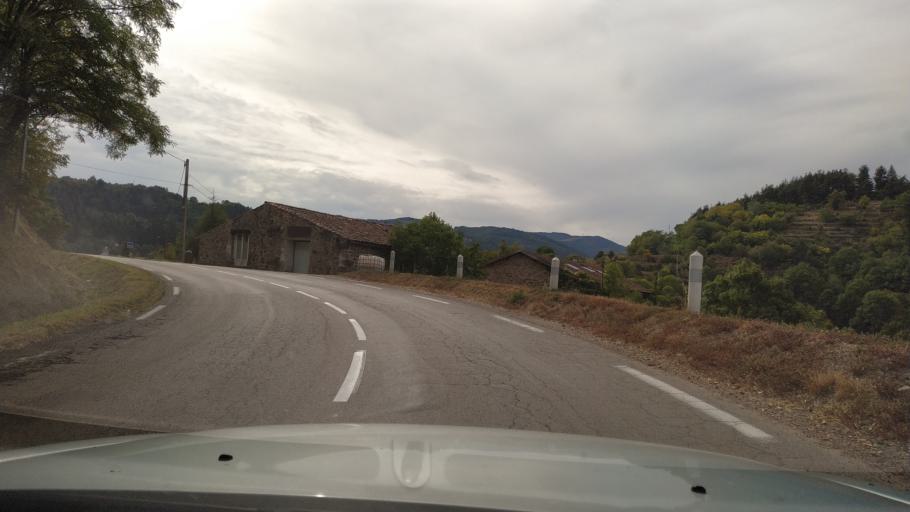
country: FR
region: Rhone-Alpes
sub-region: Departement de l'Ardeche
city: Lamastre
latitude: 44.9884
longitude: 4.5635
